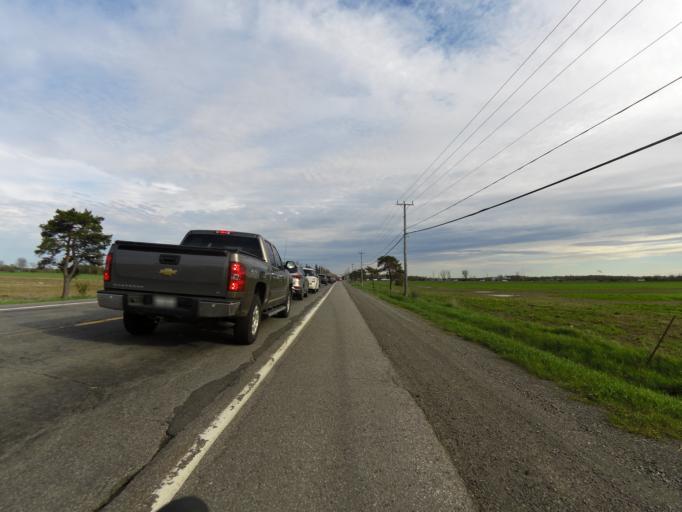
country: CA
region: Ontario
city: Ottawa
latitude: 45.3095
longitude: -75.7097
